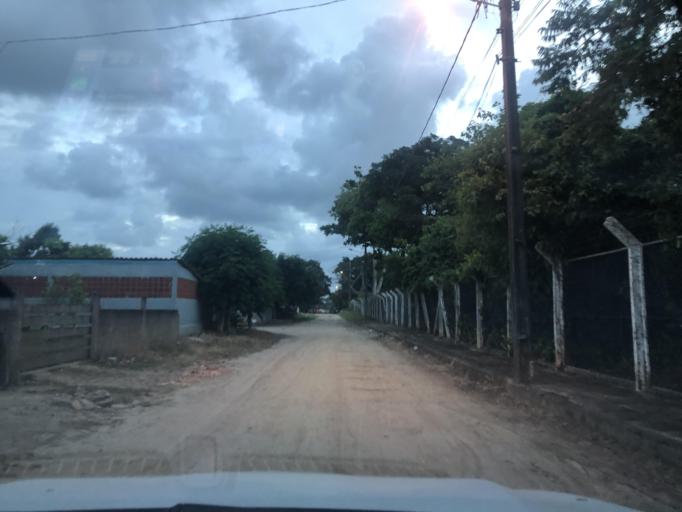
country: BR
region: Santa Catarina
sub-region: Sao Francisco Do Sul
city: Sao Francisco do Sul
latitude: -26.2277
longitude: -48.5262
